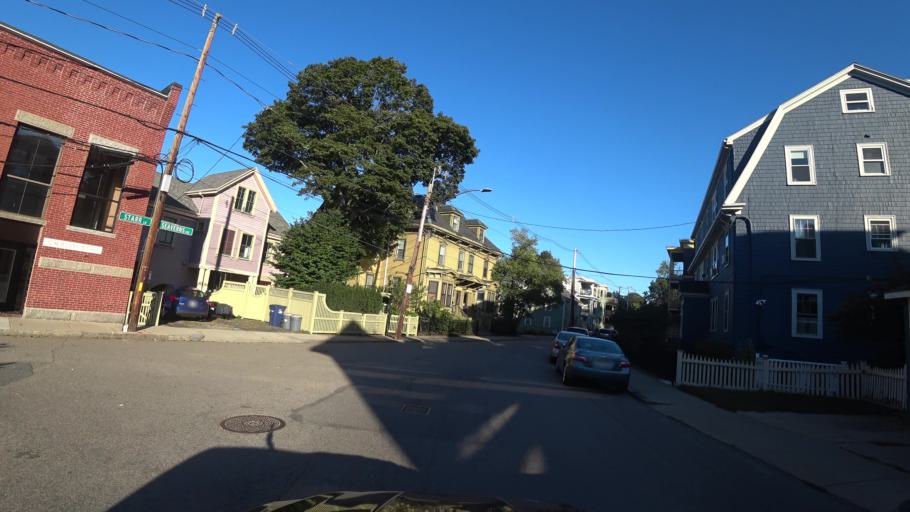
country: US
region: Massachusetts
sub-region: Suffolk County
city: Jamaica Plain
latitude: 42.3119
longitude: -71.1119
